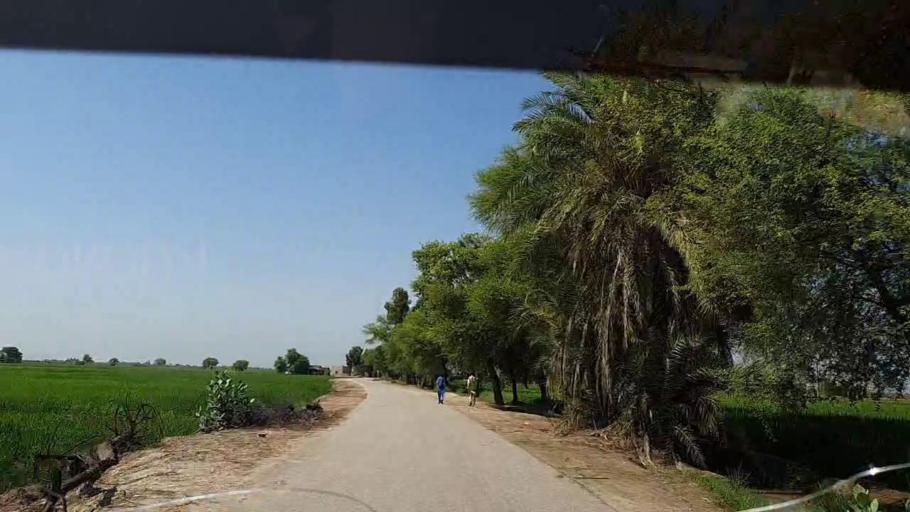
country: PK
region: Sindh
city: Kandhkot
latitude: 28.3085
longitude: 69.1055
